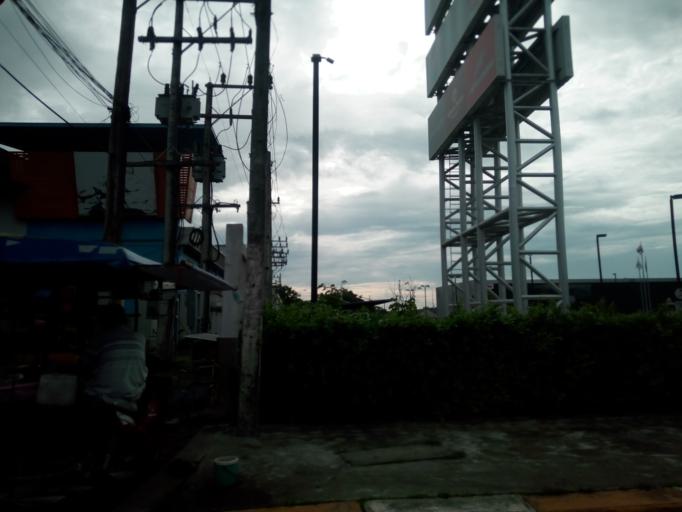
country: TH
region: Phuket
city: Thalang
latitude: 8.0054
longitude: 98.3437
